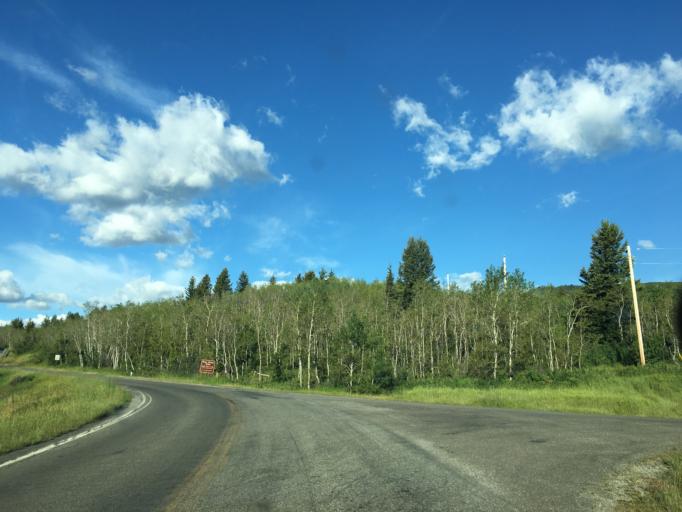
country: CA
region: Alberta
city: Cardston
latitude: 48.8566
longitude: -113.4361
